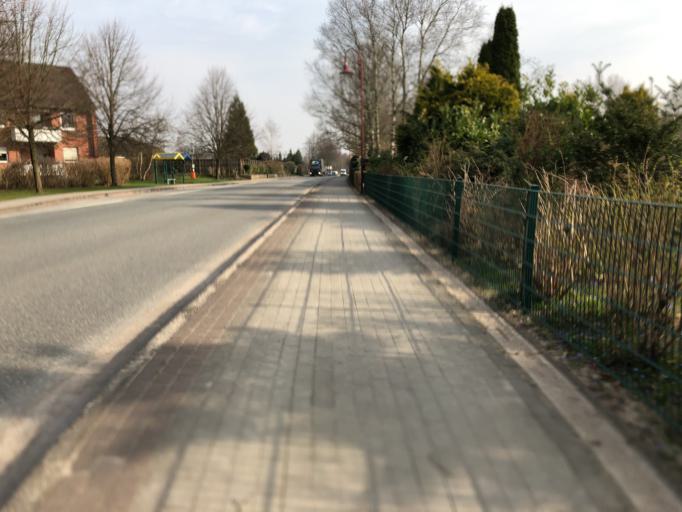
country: DE
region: Schleswig-Holstein
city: Tarp
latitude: 54.6669
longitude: 9.4080
